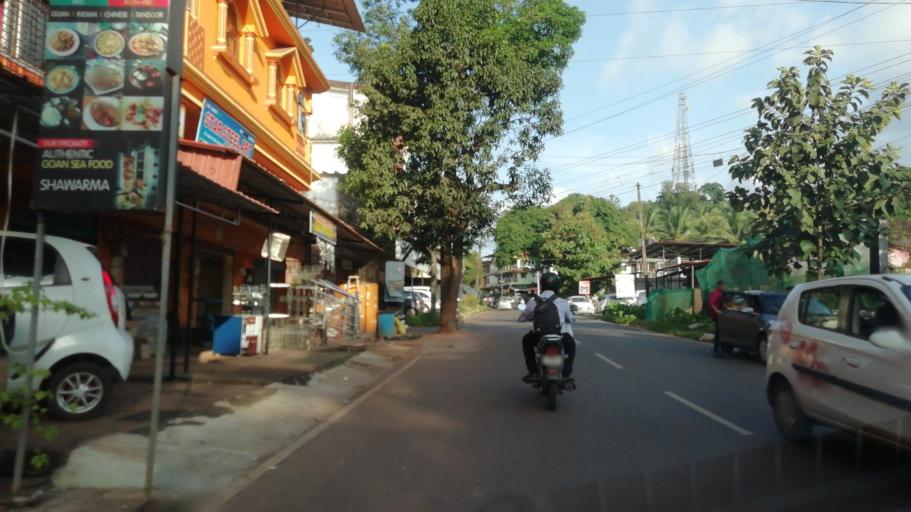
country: IN
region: Goa
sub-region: North Goa
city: Ponda
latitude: 15.3988
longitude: 74.0208
